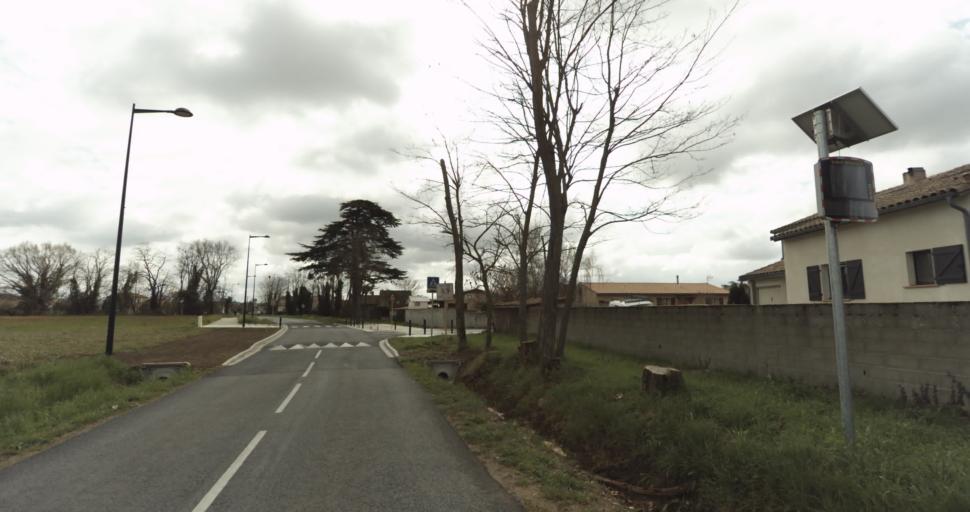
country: FR
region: Midi-Pyrenees
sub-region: Departement de la Haute-Garonne
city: Auterive
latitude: 43.3566
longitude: 1.4592
